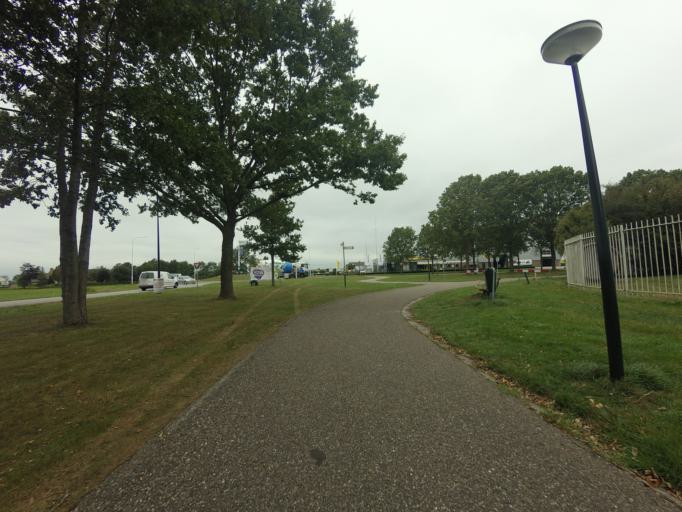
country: NL
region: Friesland
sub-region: Gemeente Opsterland
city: Gorredijk
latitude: 53.0053
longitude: 6.0517
